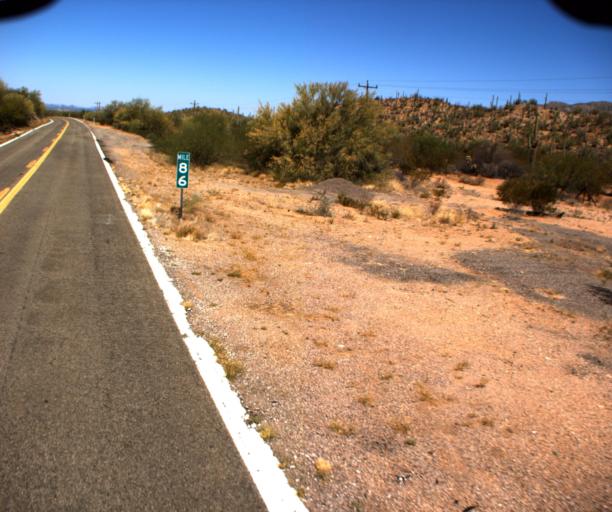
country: US
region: Arizona
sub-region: Pima County
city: Sells
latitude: 32.1733
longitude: -112.2114
